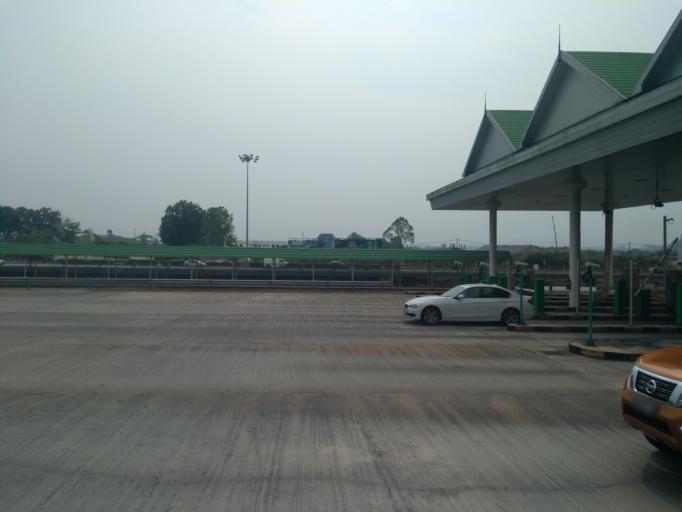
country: MY
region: Perak
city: Ipoh
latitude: 4.5851
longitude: 101.1448
